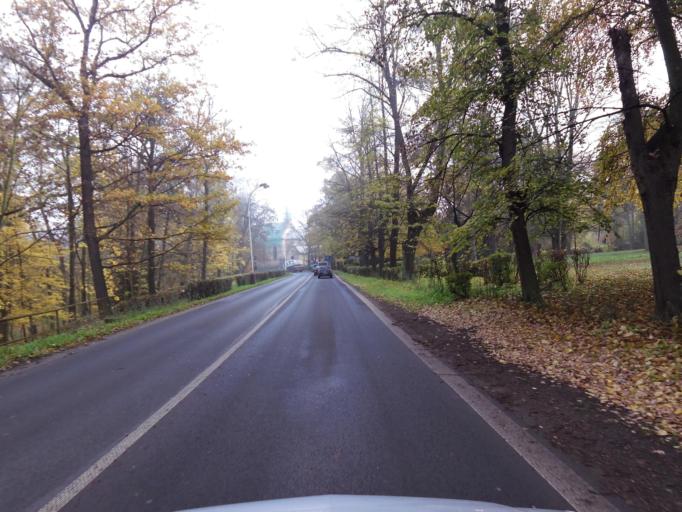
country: CZ
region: Ustecky
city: Zatec
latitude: 50.3230
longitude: 13.5382
